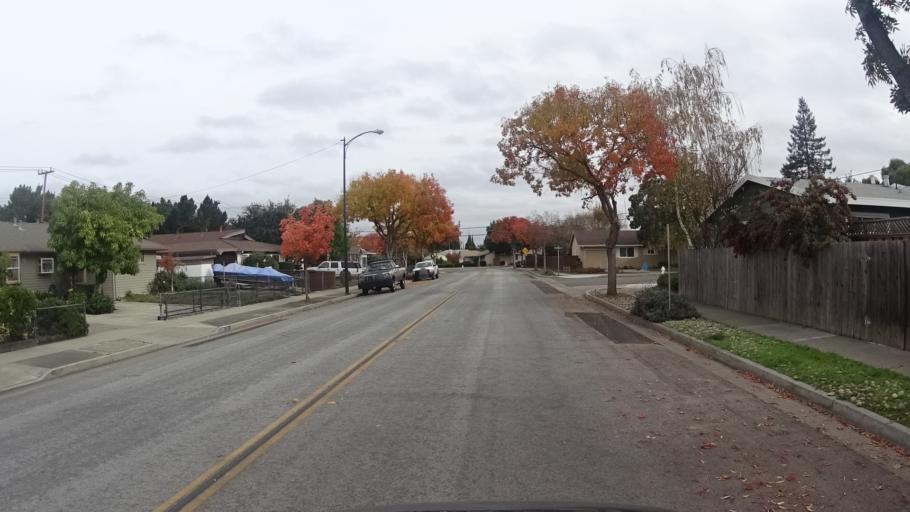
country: US
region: California
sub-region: Santa Clara County
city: Sunnyvale
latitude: 37.3708
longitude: -122.0515
